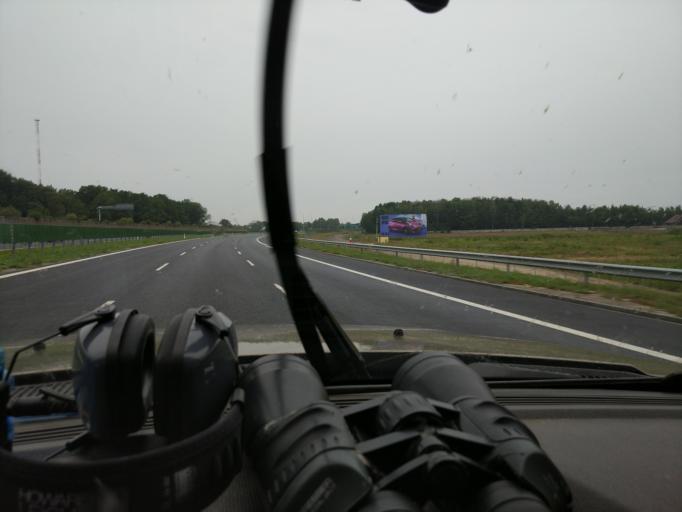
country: PL
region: Masovian Voivodeship
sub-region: Powiat wolominski
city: Slupno
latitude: 52.3459
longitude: 21.1566
